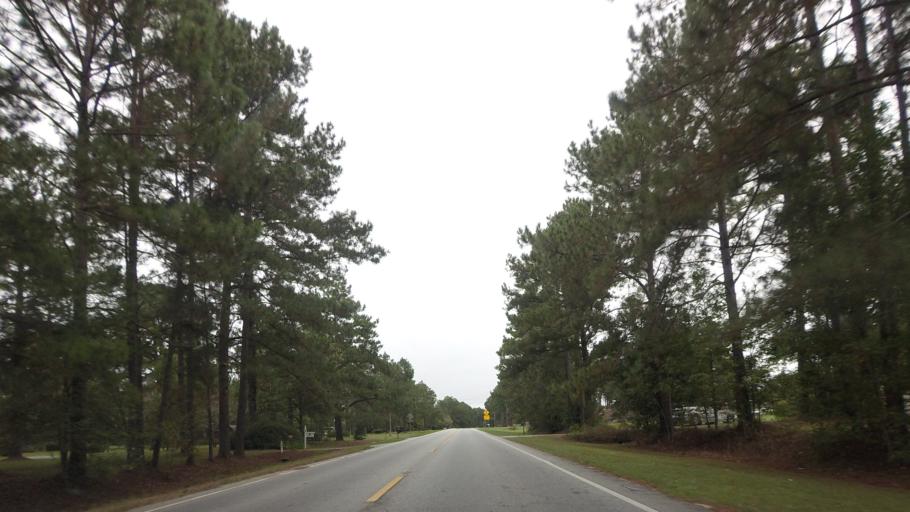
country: US
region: Georgia
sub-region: Berrien County
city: Ray City
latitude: 31.0530
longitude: -83.1980
